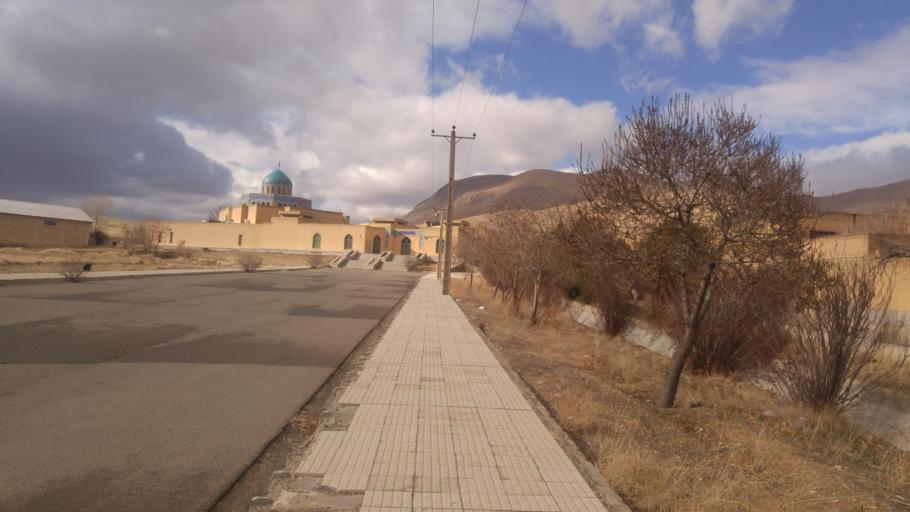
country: IR
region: Markazi
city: Shazand
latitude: 34.0465
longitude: 49.4171
